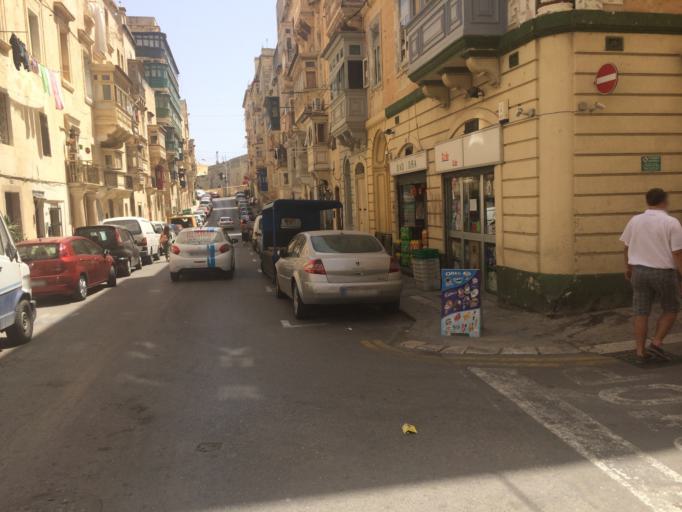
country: MT
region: Il-Belt Valletta
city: Valletta
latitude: 35.9005
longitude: 14.5163
